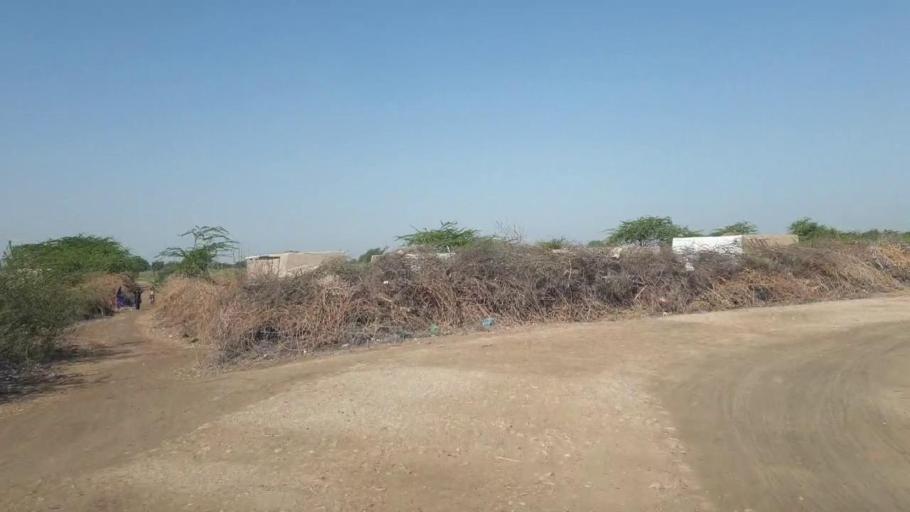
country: PK
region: Sindh
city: Umarkot
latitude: 25.2893
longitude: 69.6495
